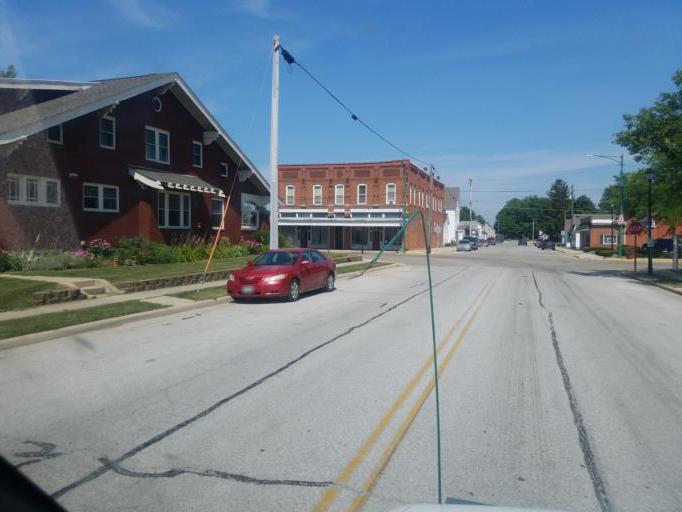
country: US
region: Ohio
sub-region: Auglaize County
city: New Bremen
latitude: 40.4945
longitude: -84.3171
